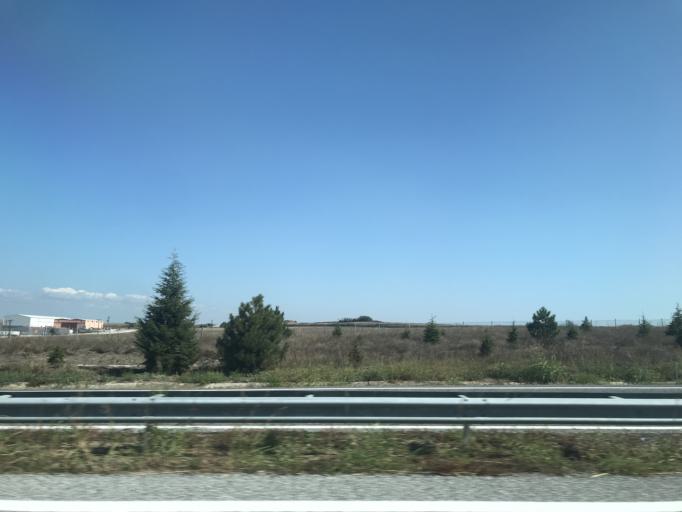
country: TR
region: Kirklareli
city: Luleburgaz
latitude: 41.4172
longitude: 27.3861
